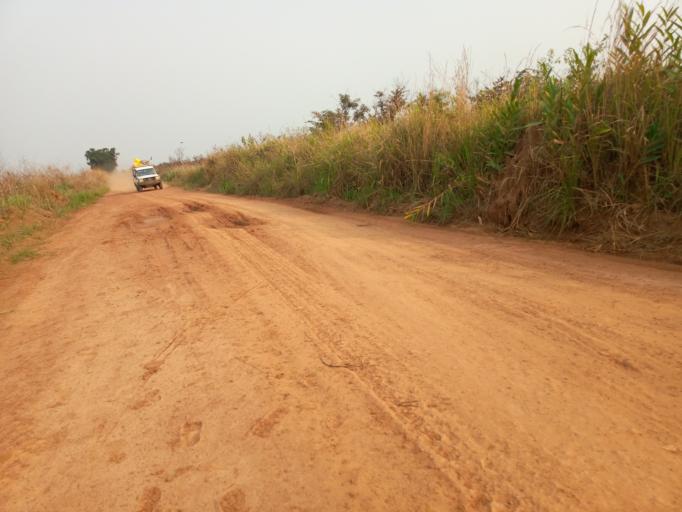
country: CD
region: Bandundu
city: Bandundu
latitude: -3.4117
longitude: 17.5987
